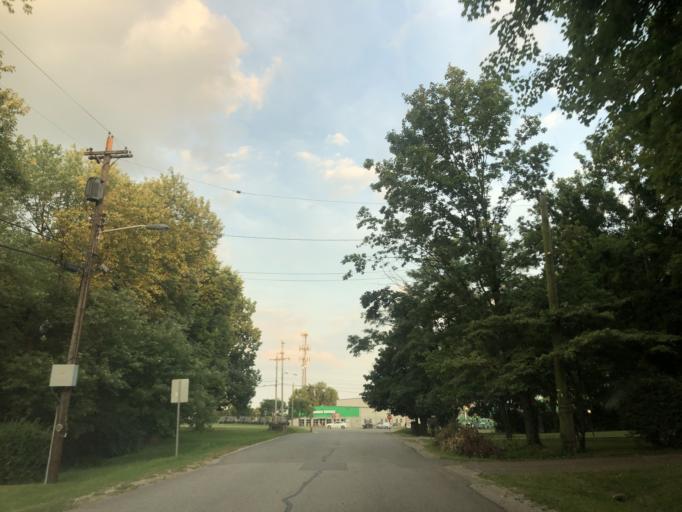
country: US
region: Tennessee
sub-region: Davidson County
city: Nashville
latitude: 36.1555
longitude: -86.7134
